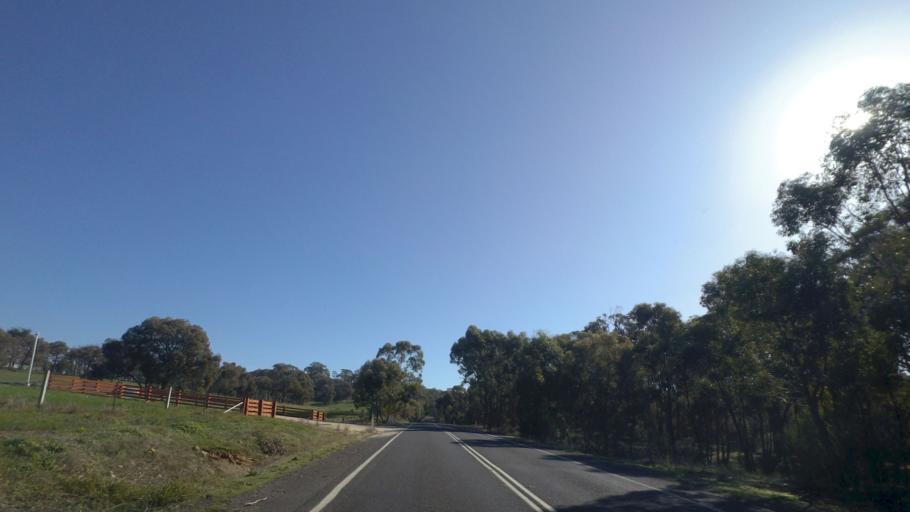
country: AU
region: Victoria
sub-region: Greater Bendigo
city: Kennington
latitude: -36.9191
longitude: 144.3386
